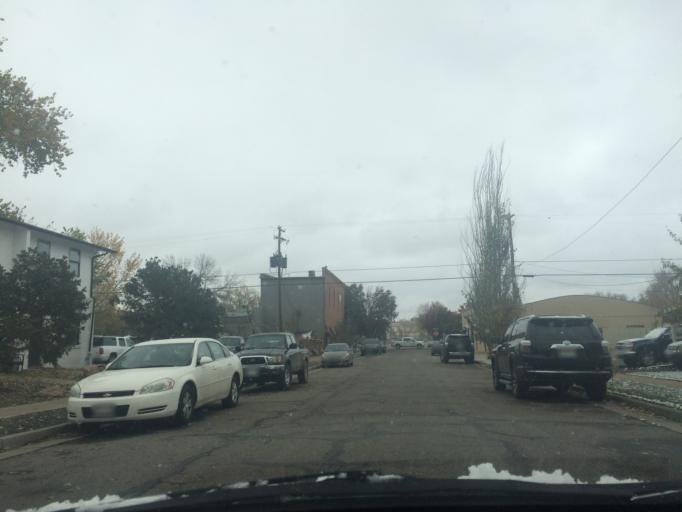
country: US
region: Colorado
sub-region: Boulder County
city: Erie
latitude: 40.0490
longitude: -105.0487
